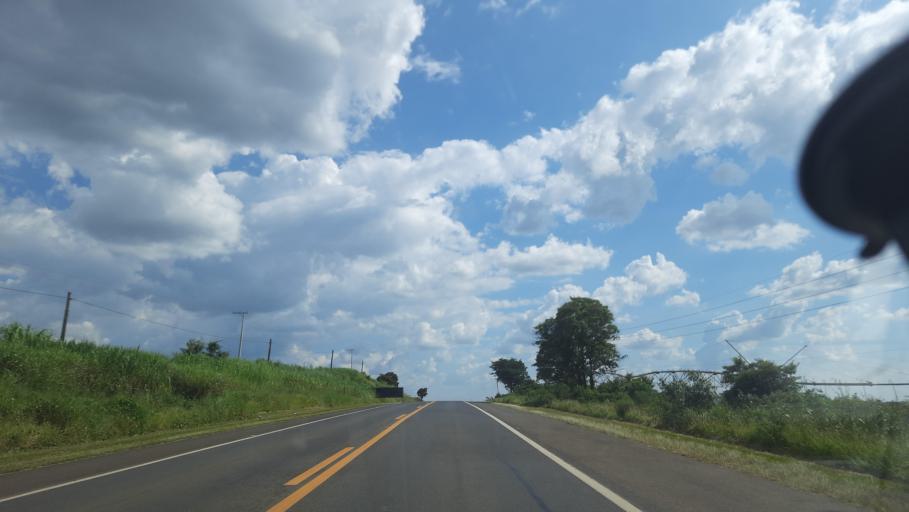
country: BR
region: Sao Paulo
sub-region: Sao Jose Do Rio Pardo
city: Sao Jose do Rio Pardo
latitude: -21.6739
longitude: -46.9238
